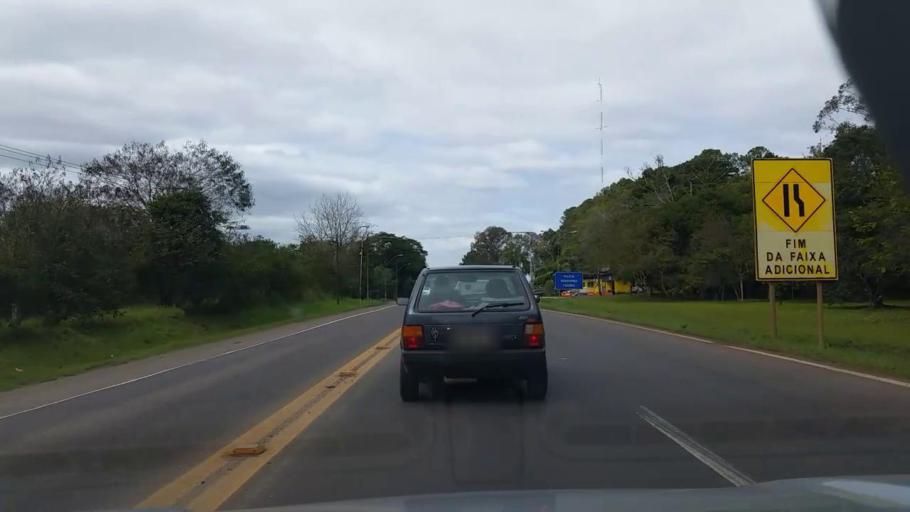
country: BR
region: Rio Grande do Sul
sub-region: Lajeado
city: Lajeado
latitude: -29.4311
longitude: -52.0131
